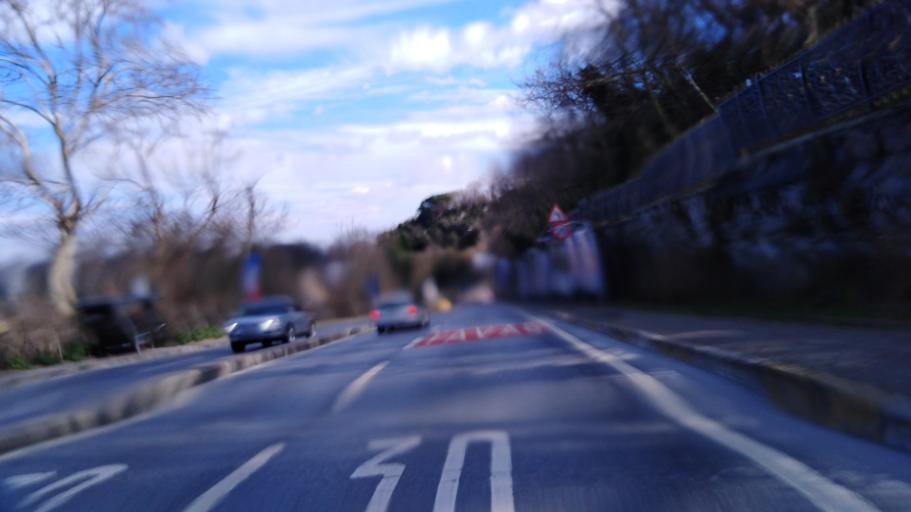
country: TR
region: Istanbul
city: Sisli
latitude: 41.1115
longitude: 29.0541
